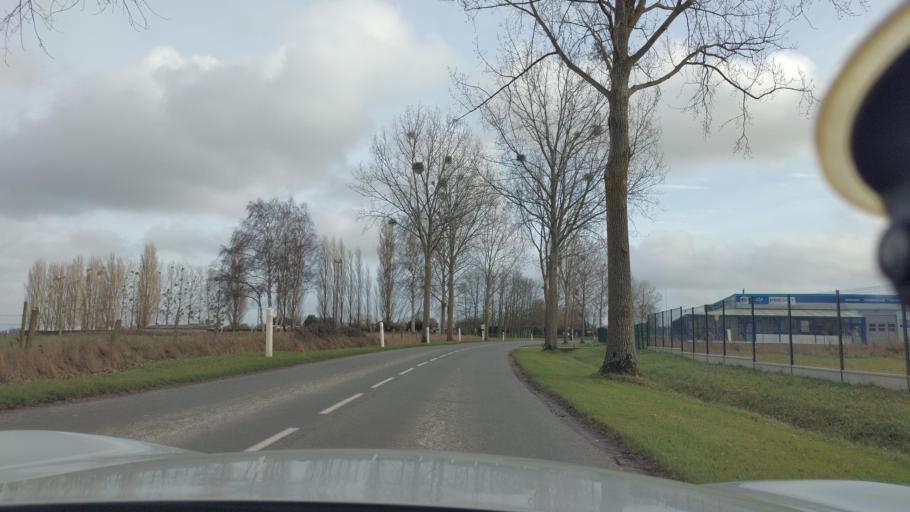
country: FR
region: Picardie
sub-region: Departement de la Somme
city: Hornoy-le-Bourg
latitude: 49.8508
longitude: 1.8917
